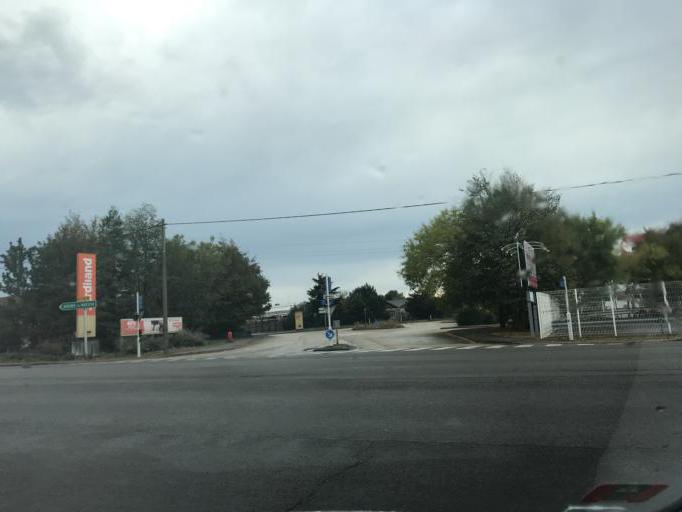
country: FR
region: Rhone-Alpes
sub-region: Departement de l'Ain
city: Bourg-en-Bresse
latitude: 46.2222
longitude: 5.2093
